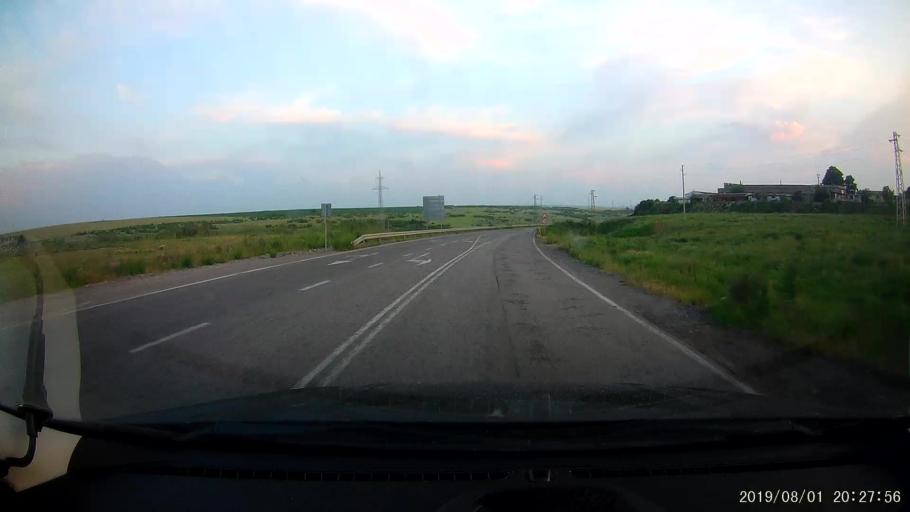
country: BG
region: Yambol
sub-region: Obshtina Elkhovo
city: Elkhovo
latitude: 42.1735
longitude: 26.5832
